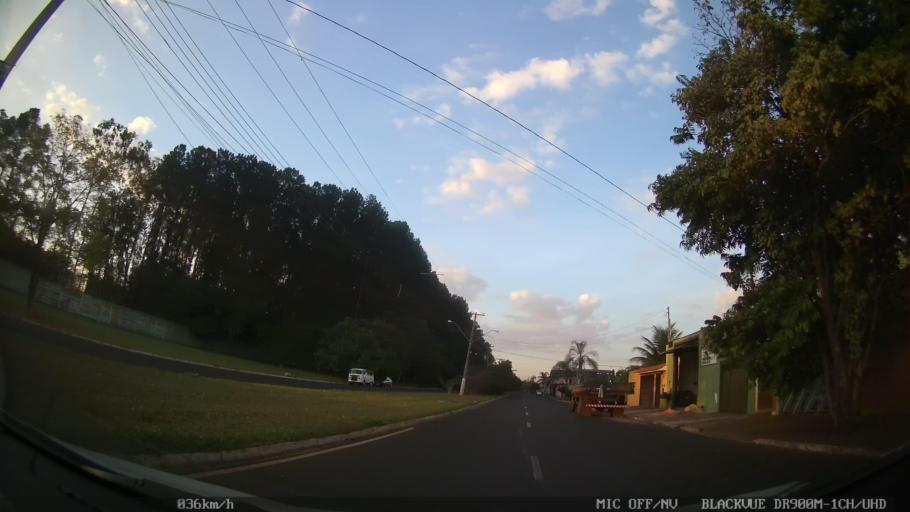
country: BR
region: Sao Paulo
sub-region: Ribeirao Preto
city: Ribeirao Preto
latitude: -21.1297
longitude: -47.8355
